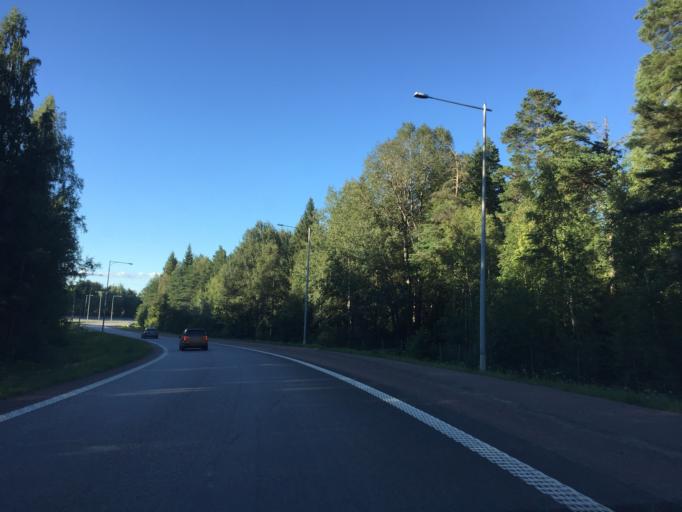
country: SE
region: OErebro
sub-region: Orebro Kommun
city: Orebro
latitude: 59.2448
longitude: 15.1483
